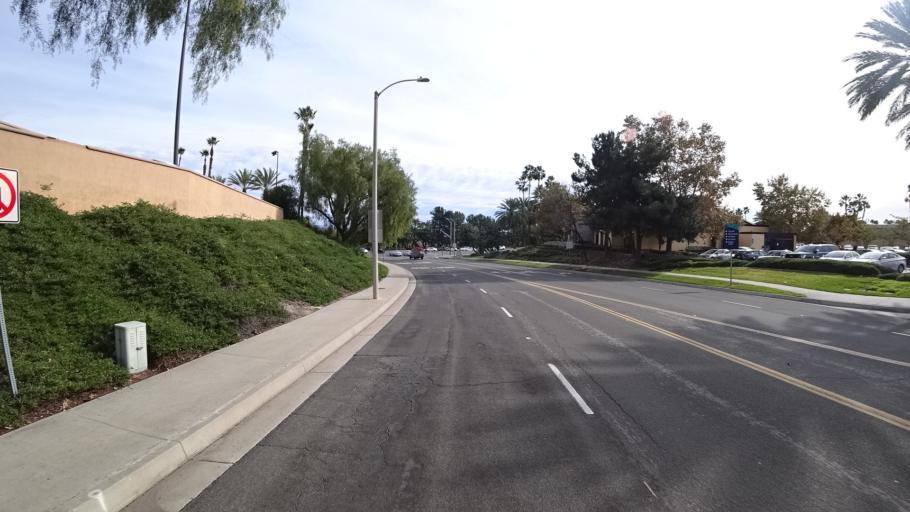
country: US
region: California
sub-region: Orange County
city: Aliso Viejo
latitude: 33.5769
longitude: -117.7245
